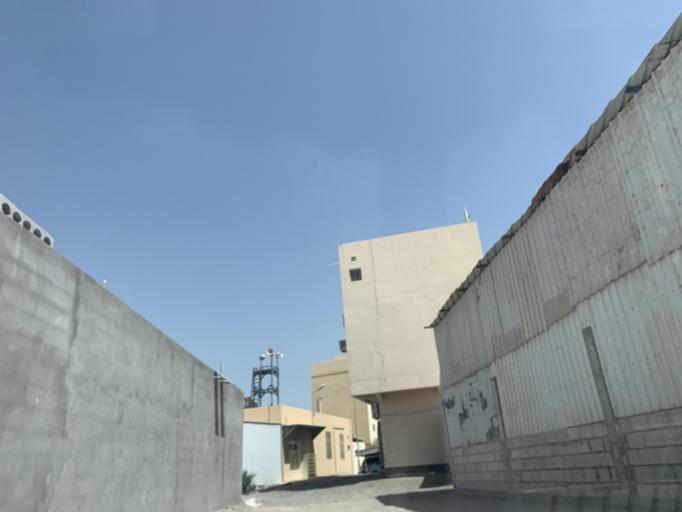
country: BH
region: Northern
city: Sitrah
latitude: 26.1600
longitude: 50.6131
